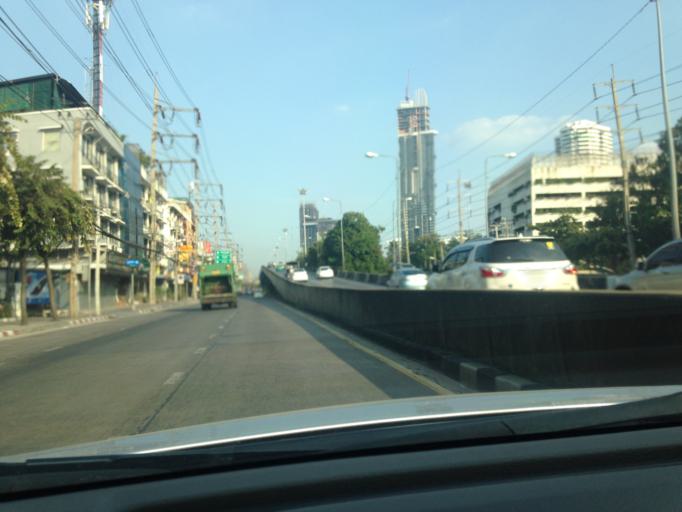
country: TH
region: Bangkok
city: Bang Kho Laem
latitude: 13.6900
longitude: 100.5064
